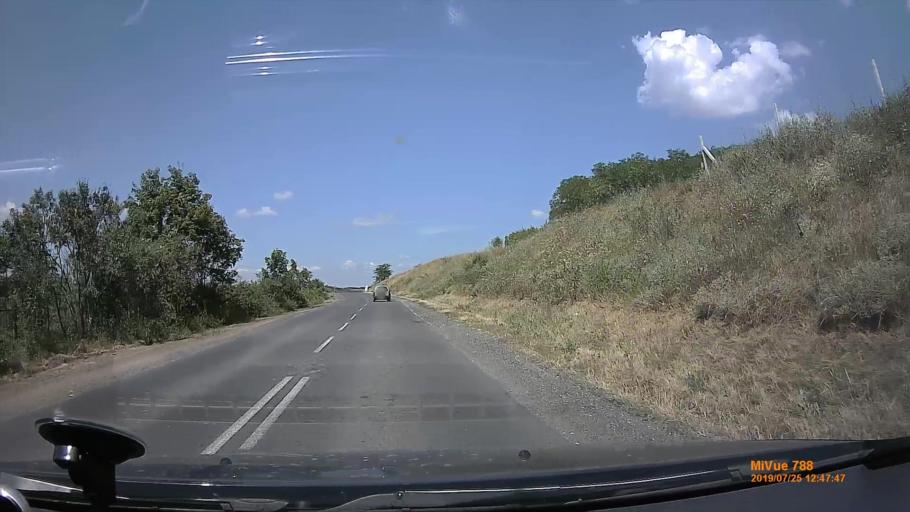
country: HU
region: Borsod-Abauj-Zemplen
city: Abaujszanto
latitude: 48.2633
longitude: 21.1861
